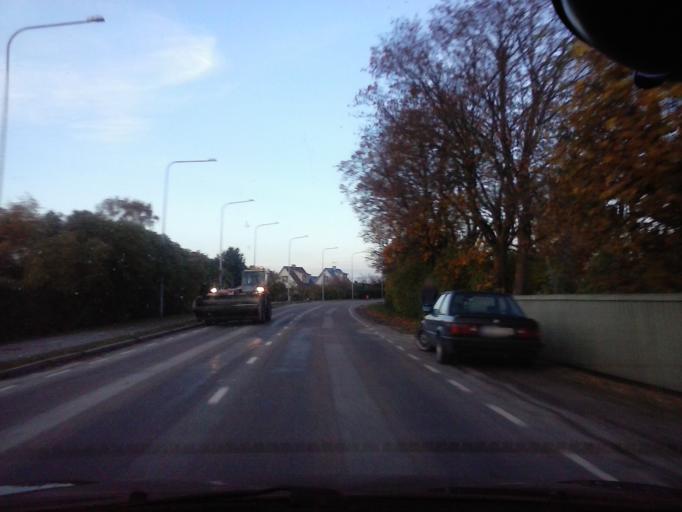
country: EE
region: Raplamaa
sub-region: Maerjamaa vald
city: Marjamaa
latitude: 58.9150
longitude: 24.4360
